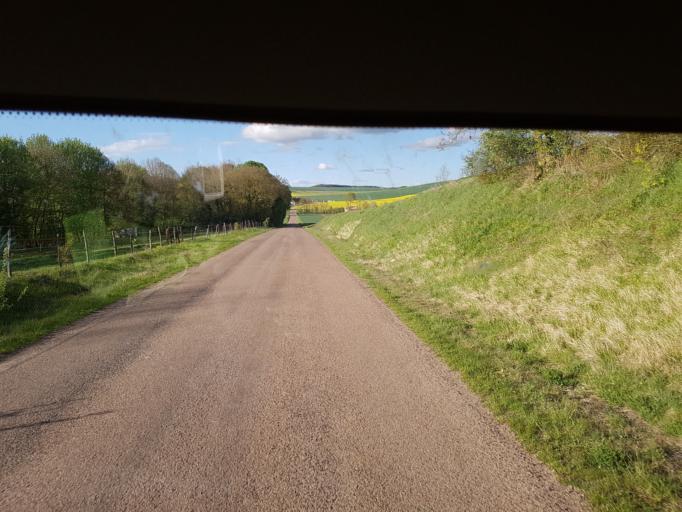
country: FR
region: Champagne-Ardenne
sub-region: Departement de l'Aube
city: Aix-en-Othe
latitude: 48.1956
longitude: 3.6338
